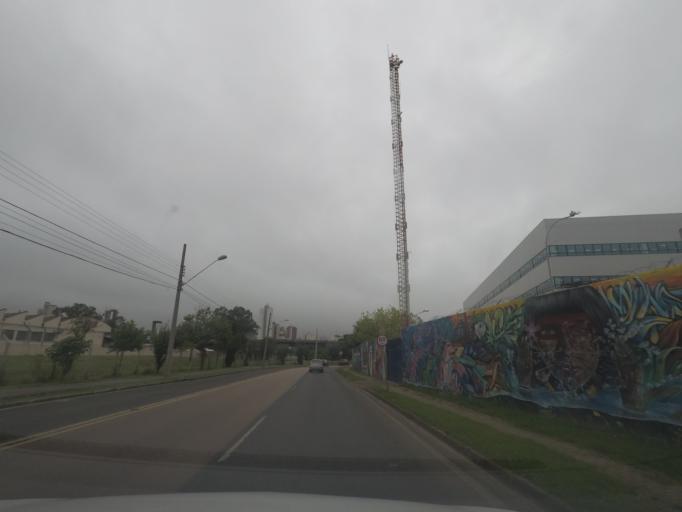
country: BR
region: Parana
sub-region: Curitiba
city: Curitiba
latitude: -25.4402
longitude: -49.2597
